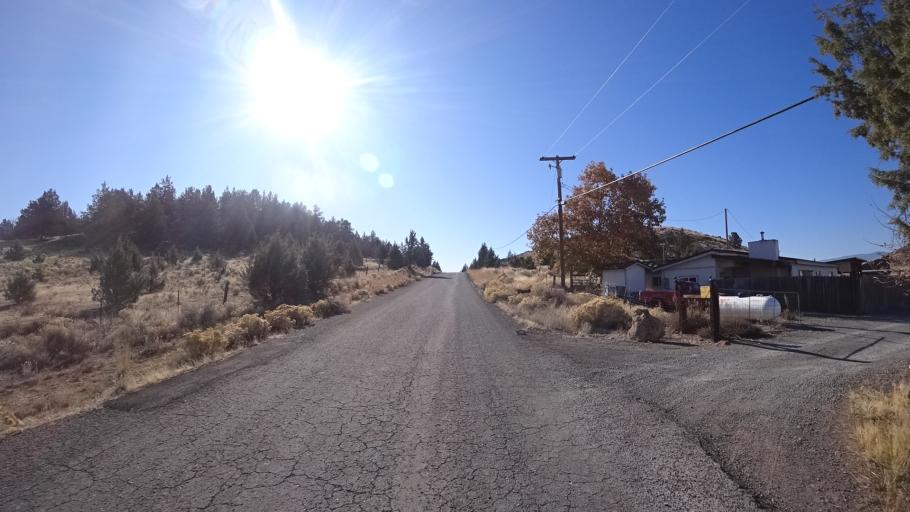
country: US
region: California
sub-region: Siskiyou County
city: Montague
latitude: 41.6999
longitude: -122.4377
